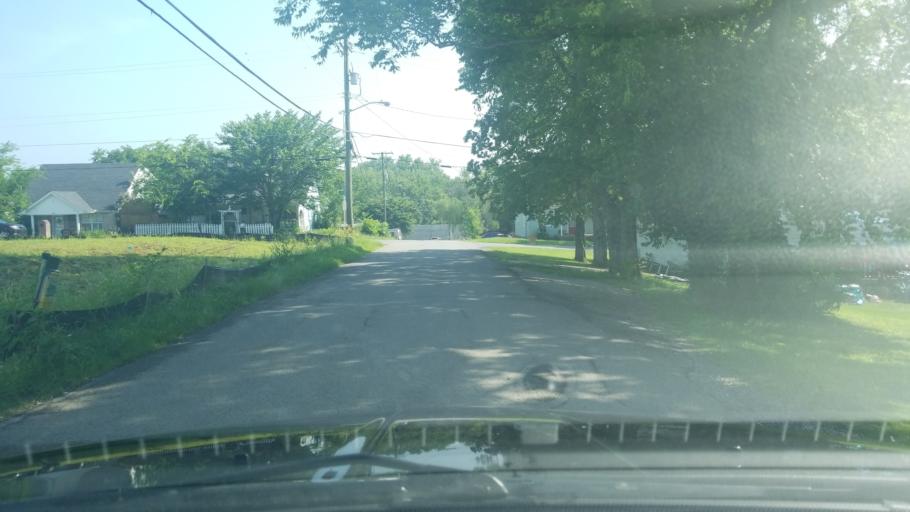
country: US
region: Tennessee
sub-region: Davidson County
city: Belle Meade
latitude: 36.1561
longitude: -86.8623
